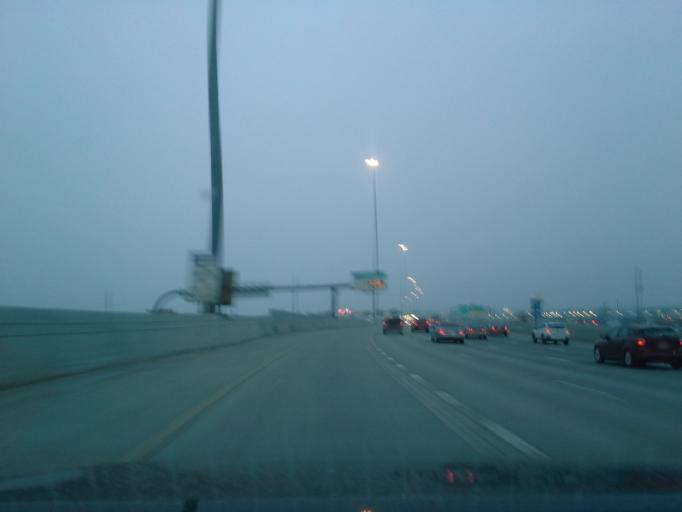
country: US
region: Utah
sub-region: Salt Lake County
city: Salt Lake City
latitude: 40.7440
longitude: -111.9043
